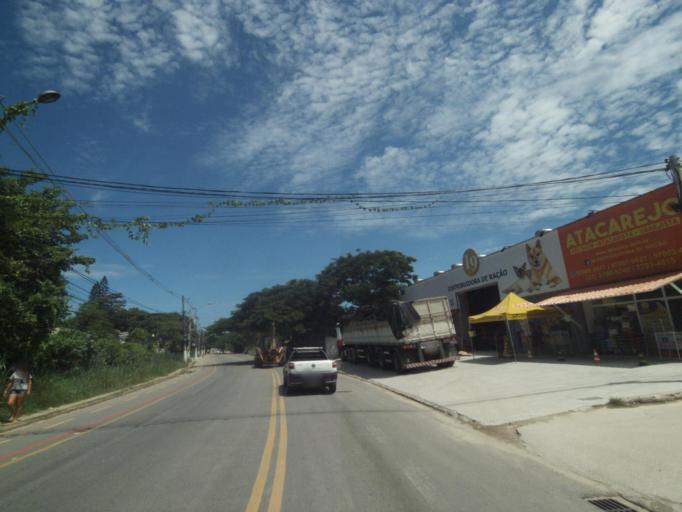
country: BR
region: Rio de Janeiro
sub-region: Niteroi
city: Niteroi
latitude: -22.9358
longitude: -43.0111
